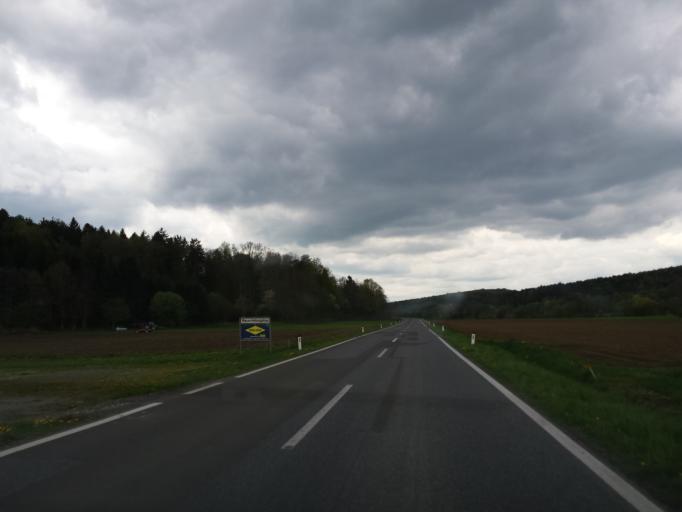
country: AT
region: Styria
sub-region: Politischer Bezirk Suedoststeiermark
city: Hatzendorf
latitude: 46.9800
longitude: 15.9995
